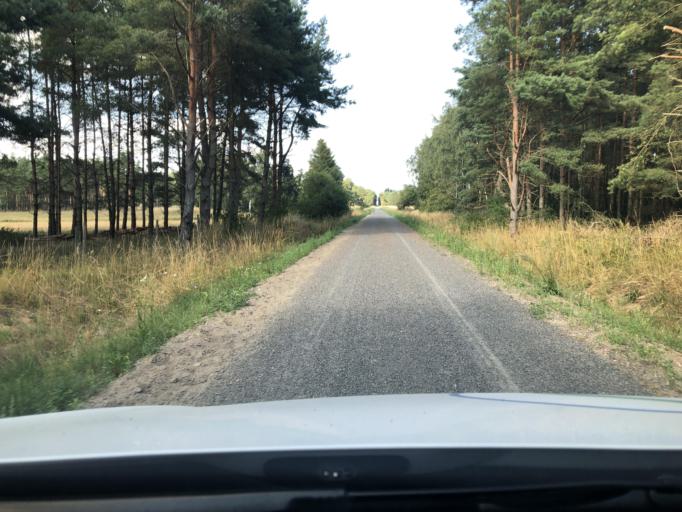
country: SE
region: Skane
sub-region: Kristianstads Kommun
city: Norra Asum
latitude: 55.9187
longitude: 14.1208
